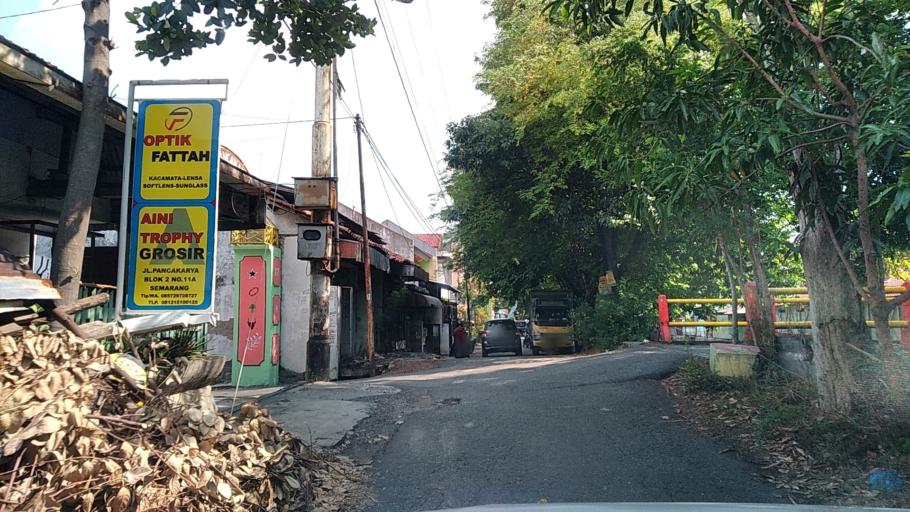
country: ID
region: Central Java
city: Semarang
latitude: -6.9831
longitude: 110.4375
